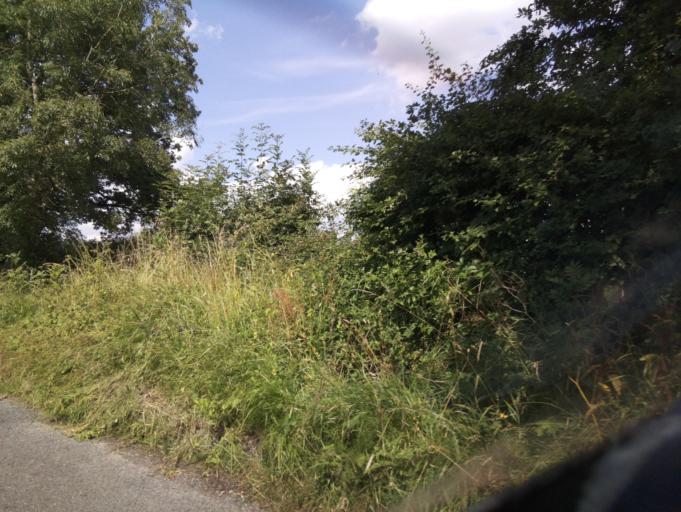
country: GB
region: England
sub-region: Hampshire
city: Kingsclere
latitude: 51.3452
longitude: -1.2811
